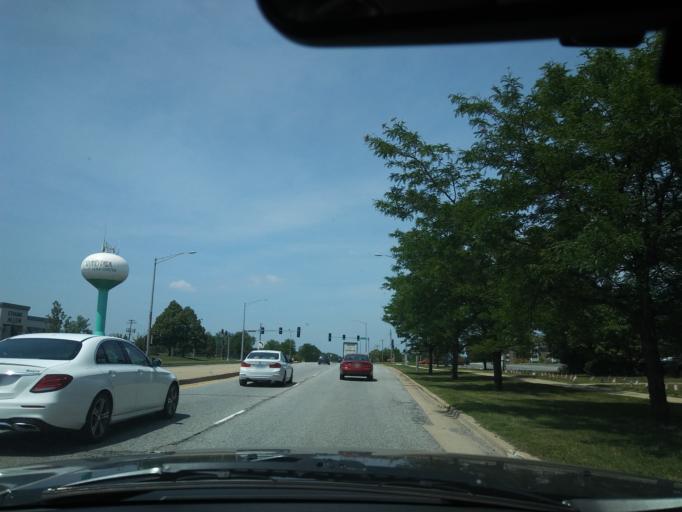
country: US
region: Illinois
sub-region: Cook County
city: Tinley Park
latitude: 41.6080
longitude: -87.7942
